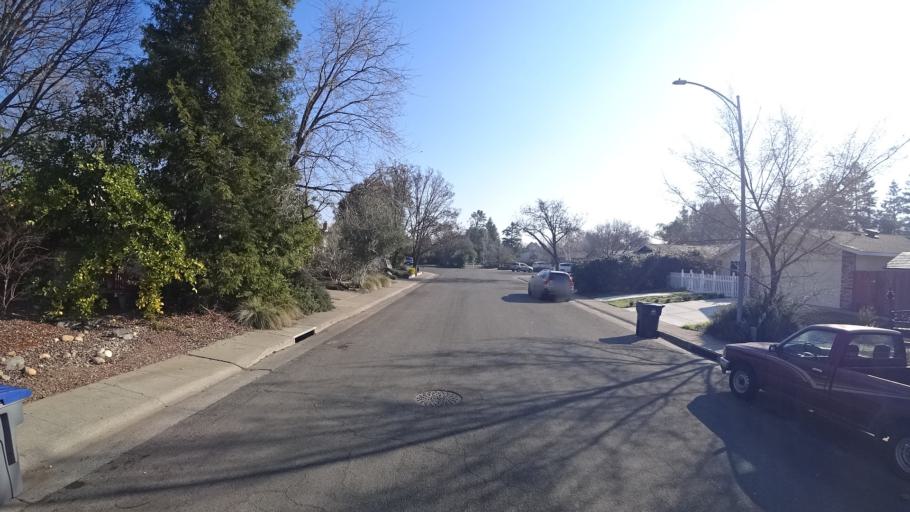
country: US
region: California
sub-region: Yolo County
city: Davis
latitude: 38.5526
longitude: -121.7840
